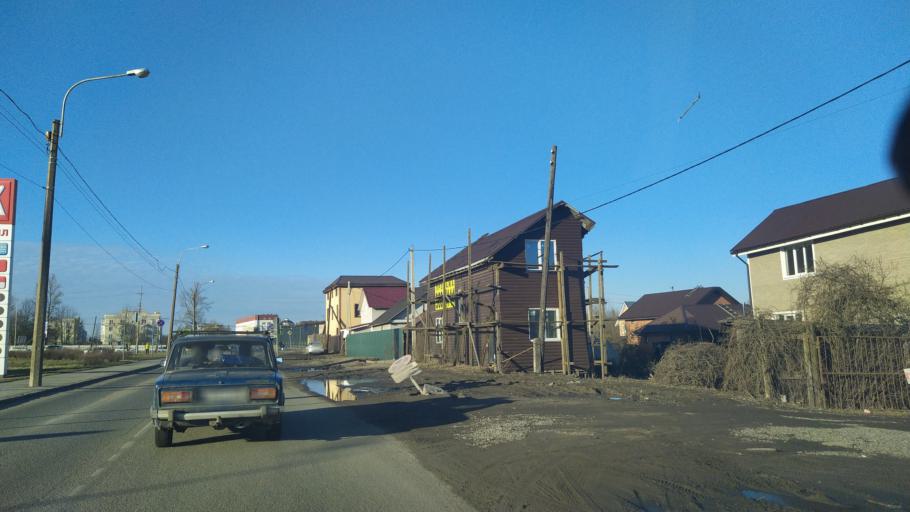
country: RU
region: St.-Petersburg
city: Pushkin
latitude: 59.6992
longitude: 30.3946
